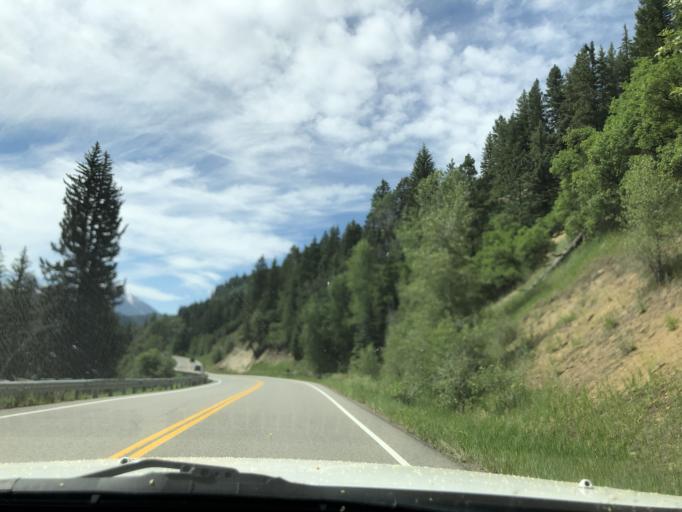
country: US
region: Colorado
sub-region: Delta County
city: Paonia
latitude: 38.9855
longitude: -107.3481
